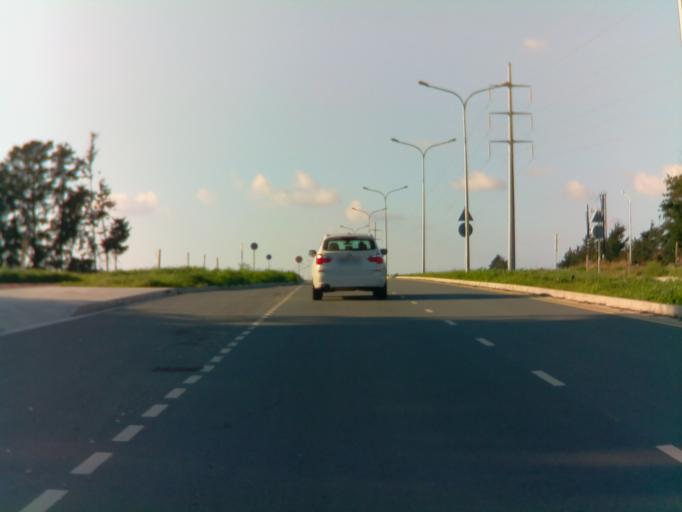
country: CY
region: Pafos
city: Paphos
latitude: 34.7357
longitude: 32.4598
